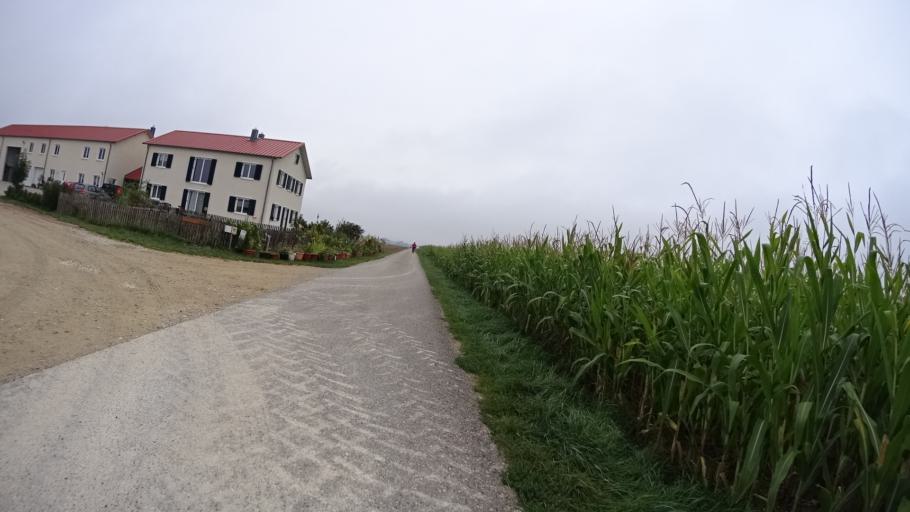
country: DE
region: Bavaria
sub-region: Upper Bavaria
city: Gaimersheim
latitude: 48.8166
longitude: 11.3818
